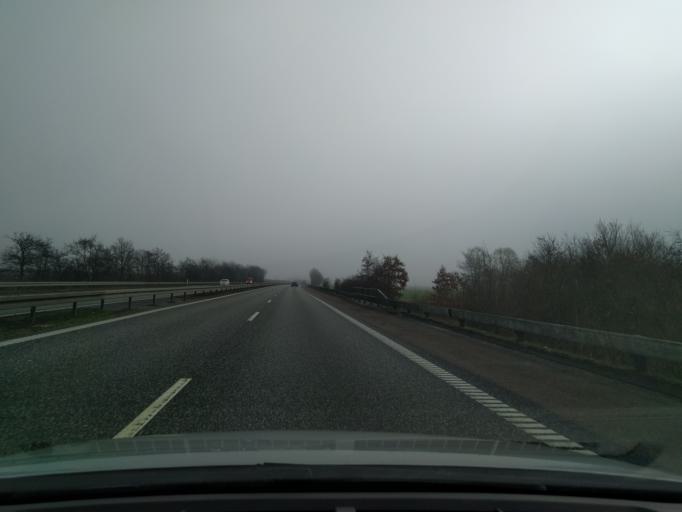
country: DK
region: Zealand
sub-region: Soro Kommune
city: Frederiksberg
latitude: 55.4467
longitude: 11.6772
